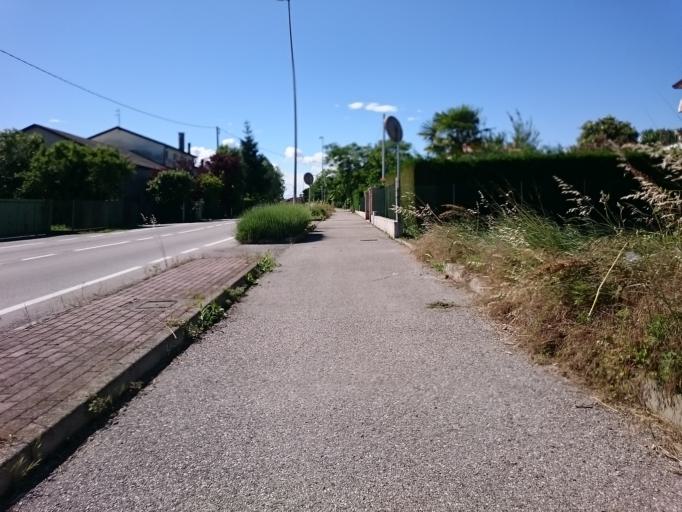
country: IT
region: Veneto
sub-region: Provincia di Venezia
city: Campolongo Maggiore
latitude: 45.3219
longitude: 12.0297
